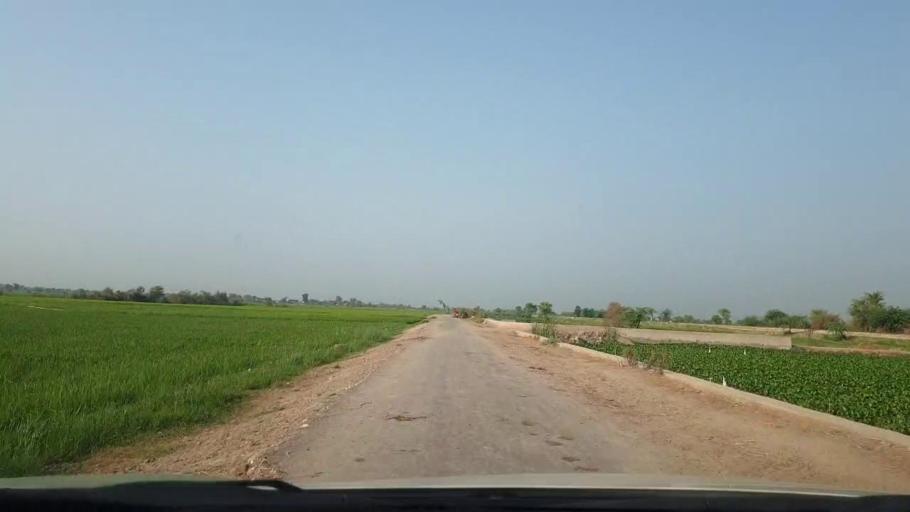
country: PK
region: Sindh
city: Larkana
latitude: 27.5021
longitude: 68.1764
